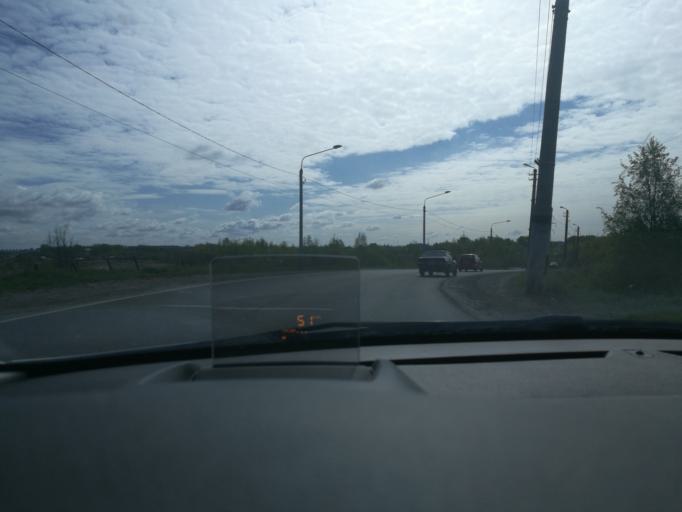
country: RU
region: Arkhangelskaya
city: Arkhangel'sk
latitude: 64.5995
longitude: 40.5541
